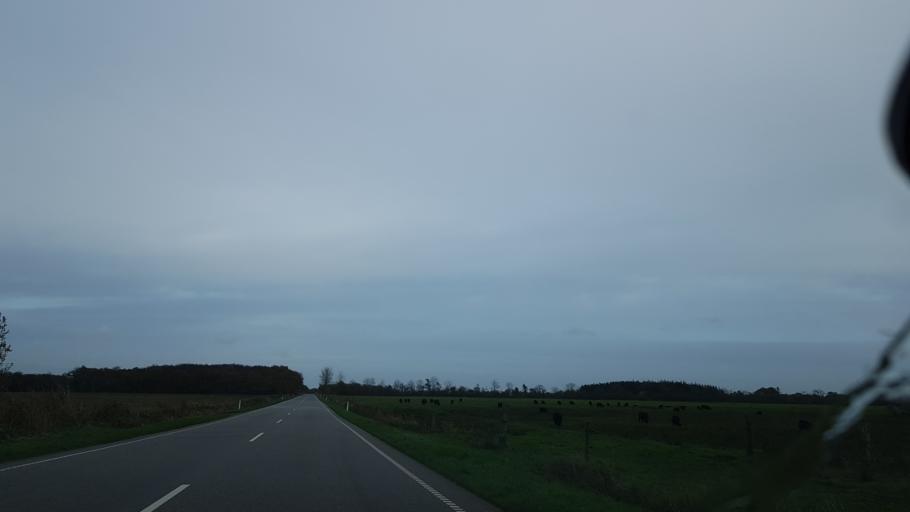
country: DK
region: South Denmark
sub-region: Tonder Kommune
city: Sherrebek
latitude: 55.1962
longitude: 8.7553
